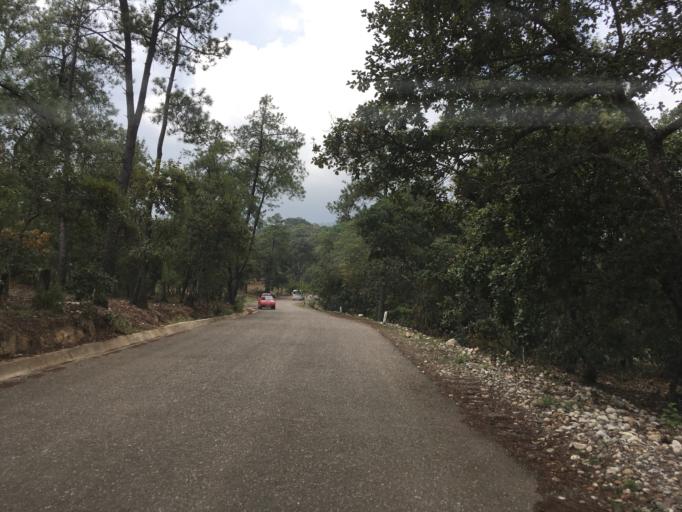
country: MX
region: Oaxaca
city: Santiago Tilantongo
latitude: 17.2209
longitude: -97.2795
